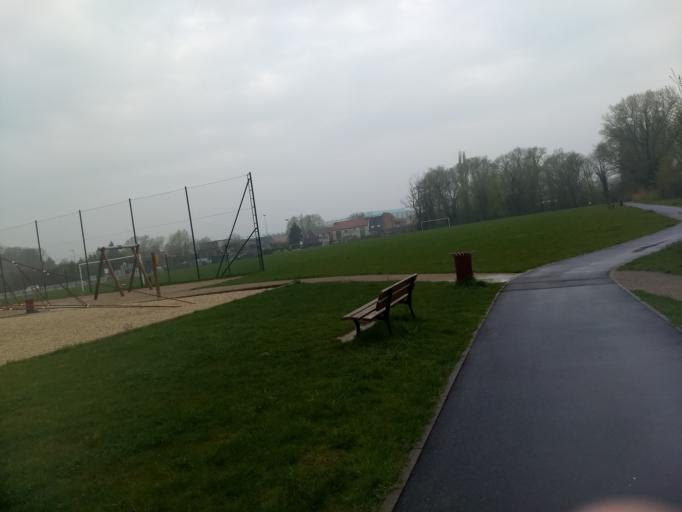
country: FR
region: Nord-Pas-de-Calais
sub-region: Departement du Pas-de-Calais
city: Biache-Saint-Vaast
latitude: 50.3092
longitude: 2.9548
